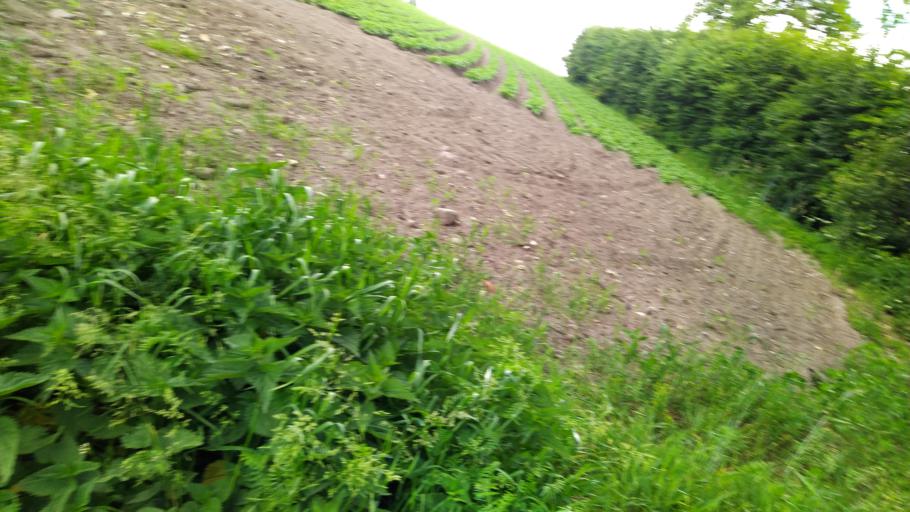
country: DE
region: Lower Saxony
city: Kutenholz
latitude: 53.4635
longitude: 9.3558
